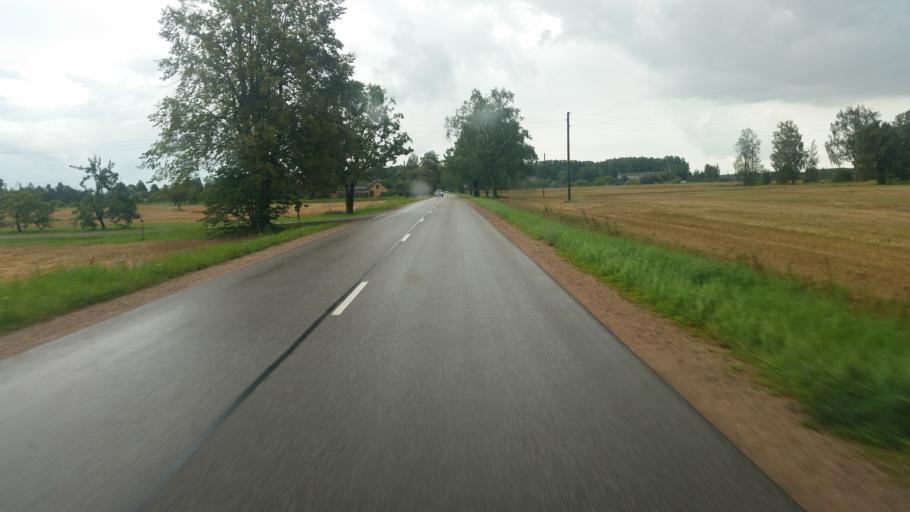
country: LV
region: Bauskas Rajons
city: Bauska
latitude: 56.4291
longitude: 24.3218
